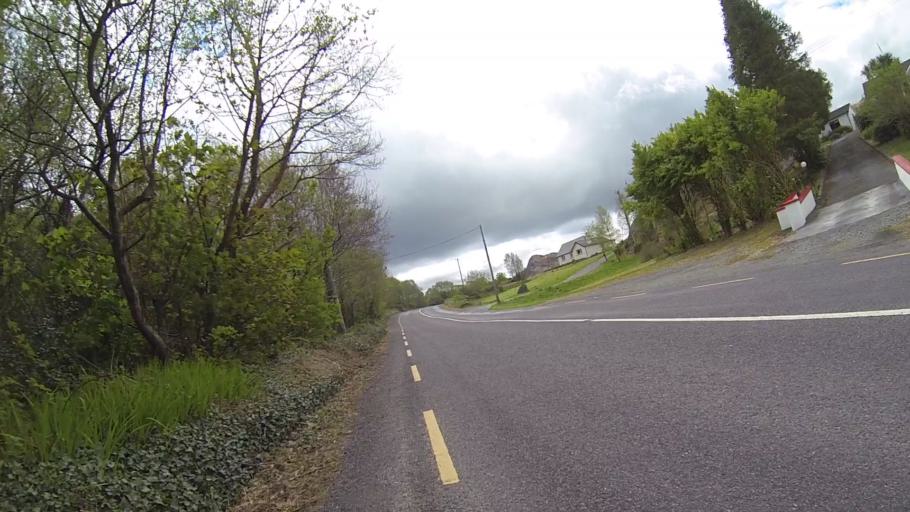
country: IE
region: Munster
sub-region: County Cork
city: Bantry
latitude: 51.7422
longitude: -9.5509
